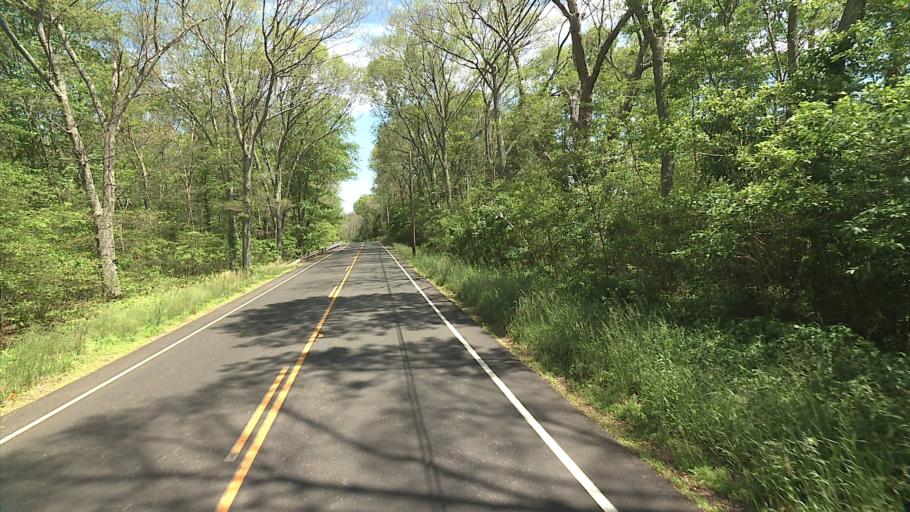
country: US
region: Connecticut
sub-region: Windham County
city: Plainfield
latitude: 41.6122
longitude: -71.8424
